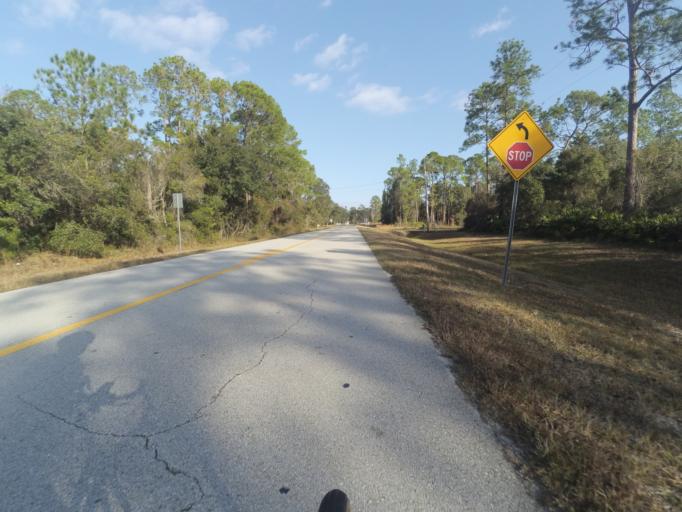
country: US
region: Florida
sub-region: Lake County
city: Astor
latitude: 29.1467
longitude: -81.5751
